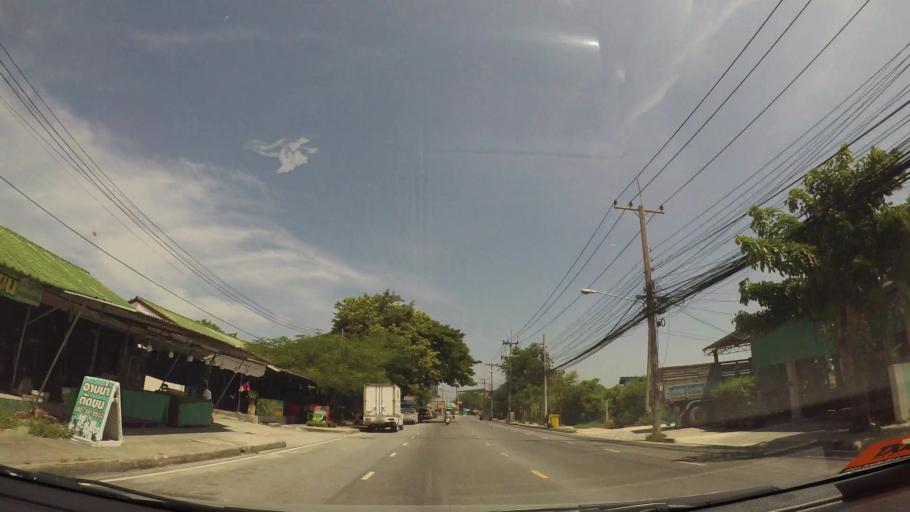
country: TH
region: Chon Buri
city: Chon Buri
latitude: 13.3254
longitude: 100.9564
